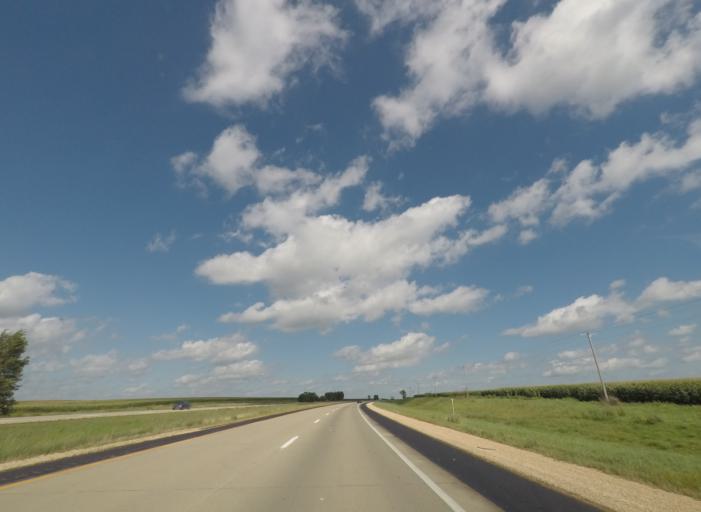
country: US
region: Iowa
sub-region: Jones County
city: Monticello
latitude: 42.2806
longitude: -91.1298
